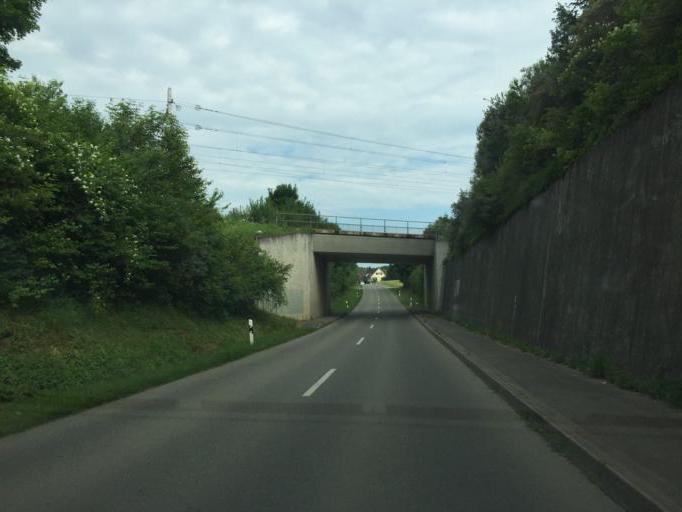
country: CH
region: Zurich
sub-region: Bezirk Andelfingen
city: Dachsen
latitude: 47.6642
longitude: 8.5977
